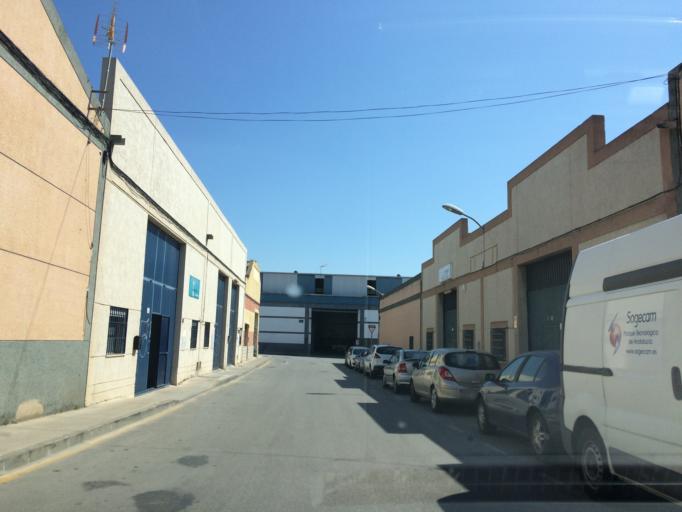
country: ES
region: Andalusia
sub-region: Provincia de Malaga
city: Malaga
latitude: 36.7024
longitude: -4.4690
